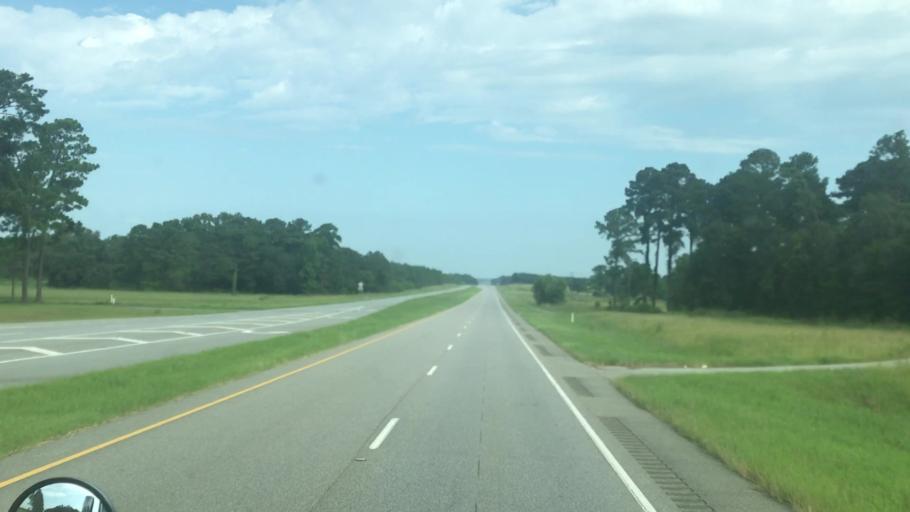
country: US
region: Georgia
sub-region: Early County
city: Blakely
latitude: 31.3219
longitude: -84.8838
